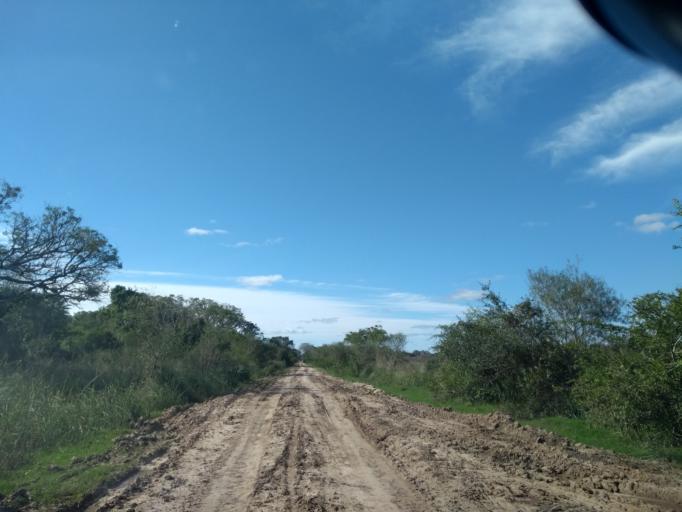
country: AR
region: Chaco
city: Margarita Belen
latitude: -27.2815
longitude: -58.9251
